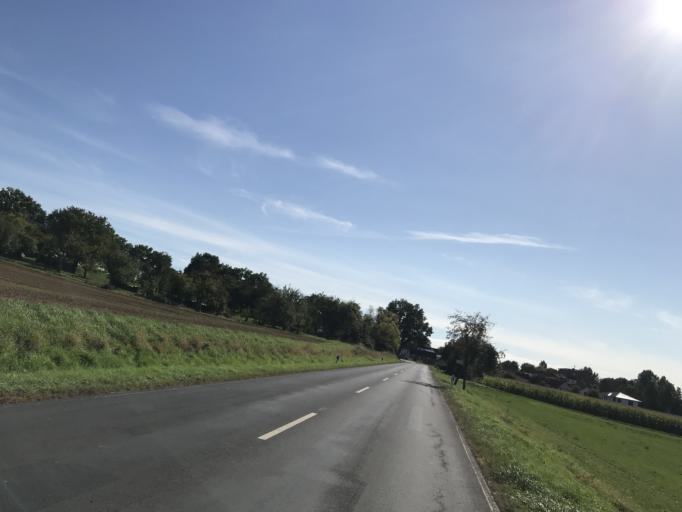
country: DE
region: Hesse
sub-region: Regierungsbezirk Darmstadt
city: Glauburg
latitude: 50.3017
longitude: 8.9908
